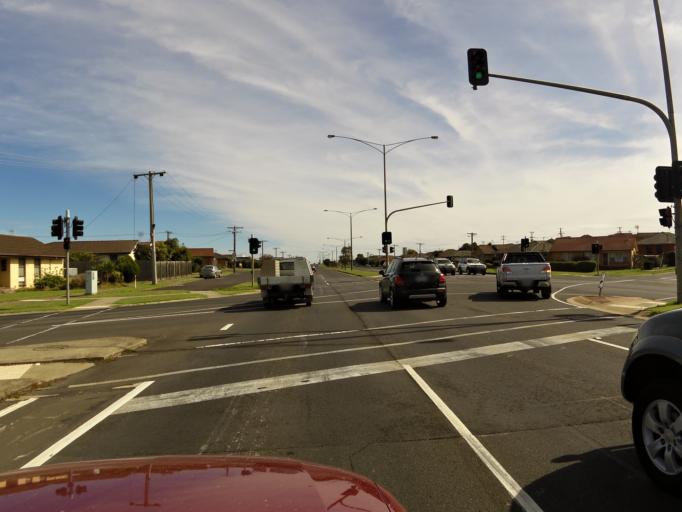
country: AU
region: Victoria
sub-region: Warrnambool
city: Warrnambool
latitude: -38.3672
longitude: 142.4642
